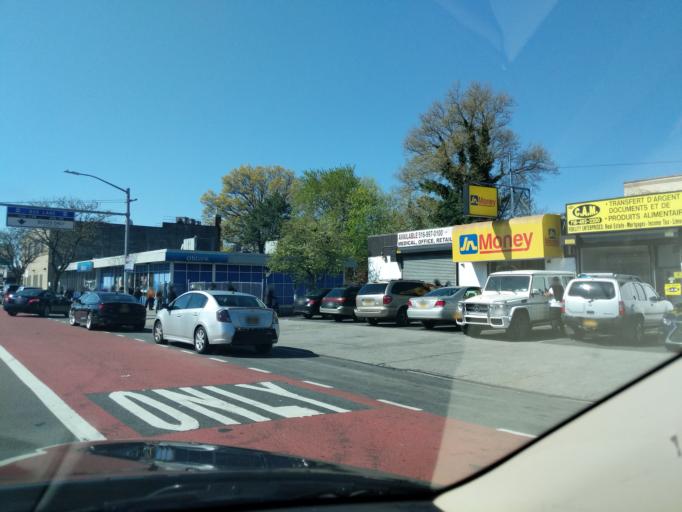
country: US
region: New York
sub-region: Kings County
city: Brooklyn
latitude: 40.6565
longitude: -73.9309
